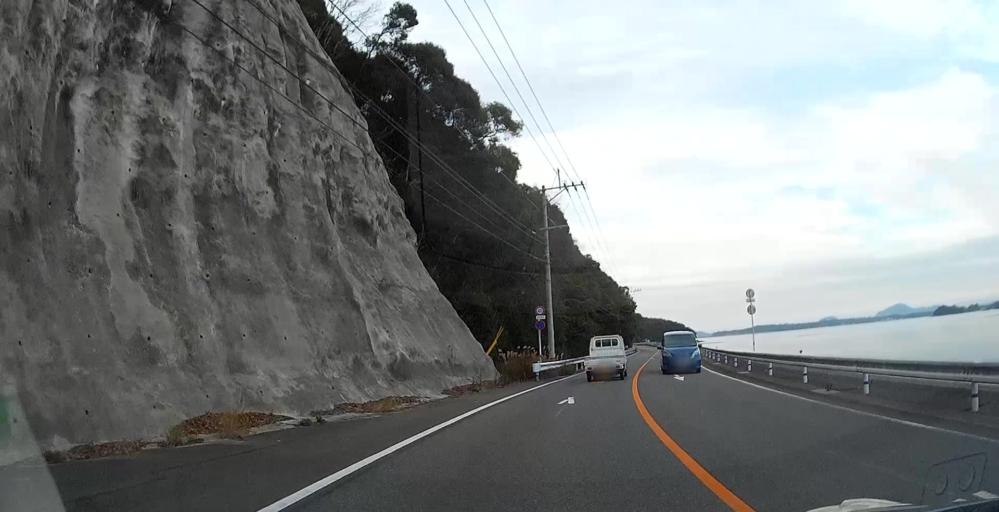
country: JP
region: Kumamoto
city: Hondo
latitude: 32.5012
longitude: 130.3911
